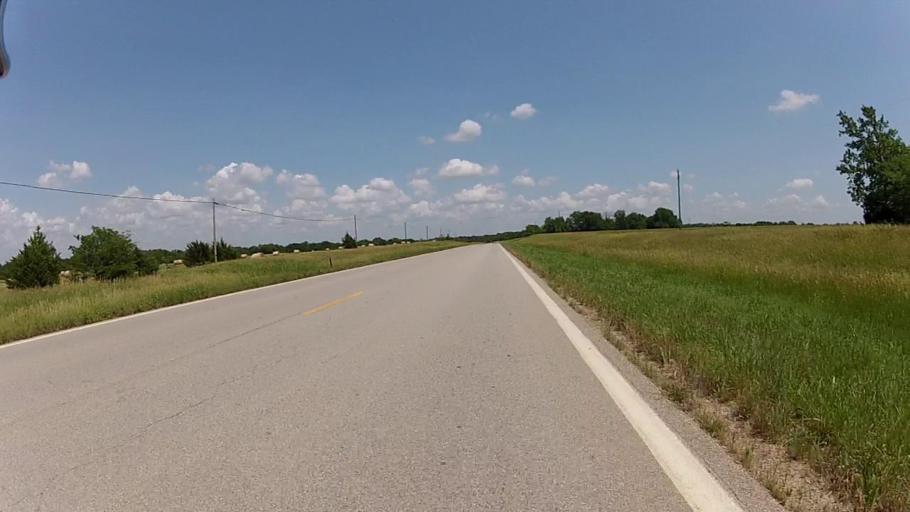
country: US
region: Kansas
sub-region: Labette County
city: Altamont
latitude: 37.1924
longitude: -95.4213
